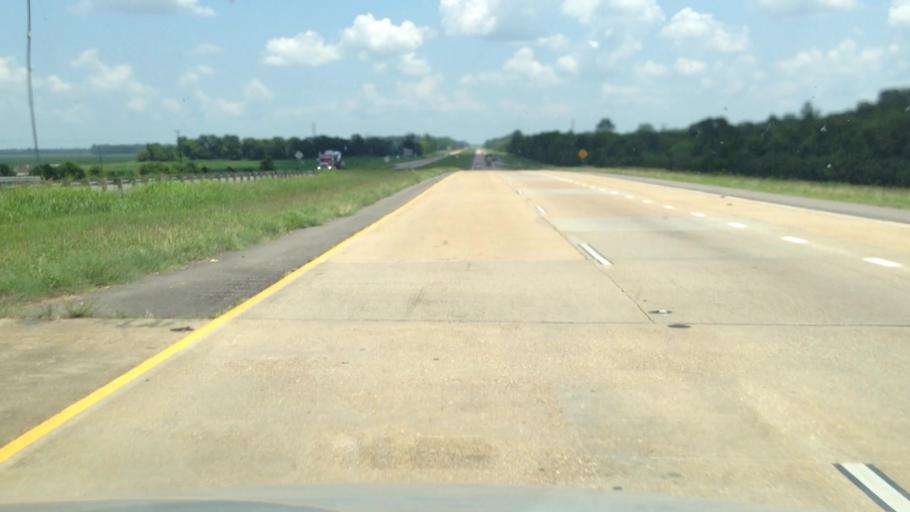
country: US
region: Louisiana
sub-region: Rapides Parish
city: Lecompte
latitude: 31.0142
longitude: -92.3753
